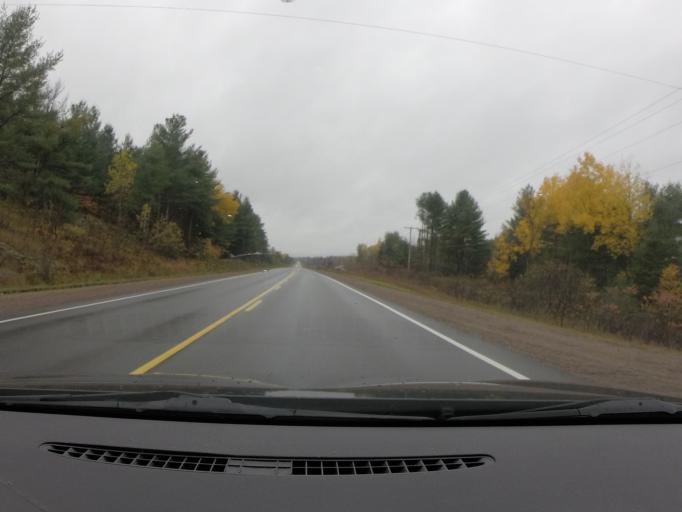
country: CA
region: Ontario
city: Skatepark
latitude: 44.6910
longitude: -77.0294
